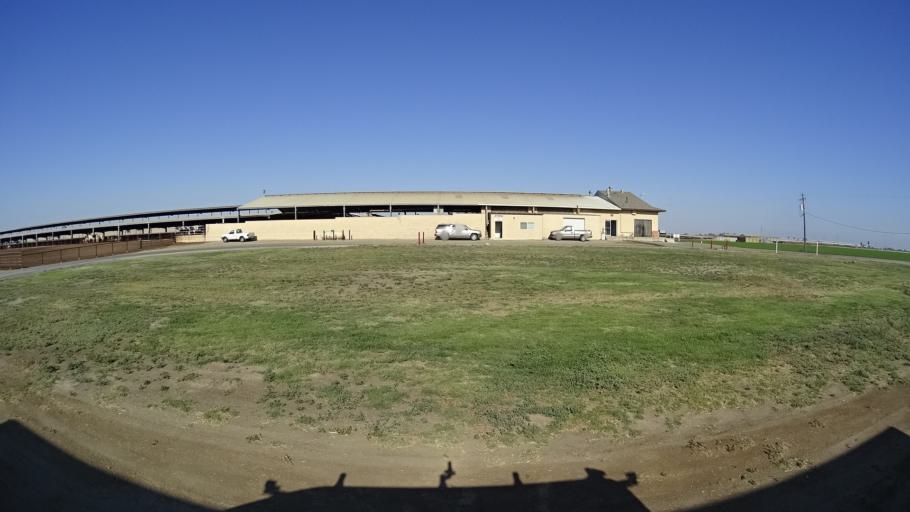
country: US
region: California
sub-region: Kings County
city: Lemoore Station
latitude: 36.3434
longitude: -119.8782
